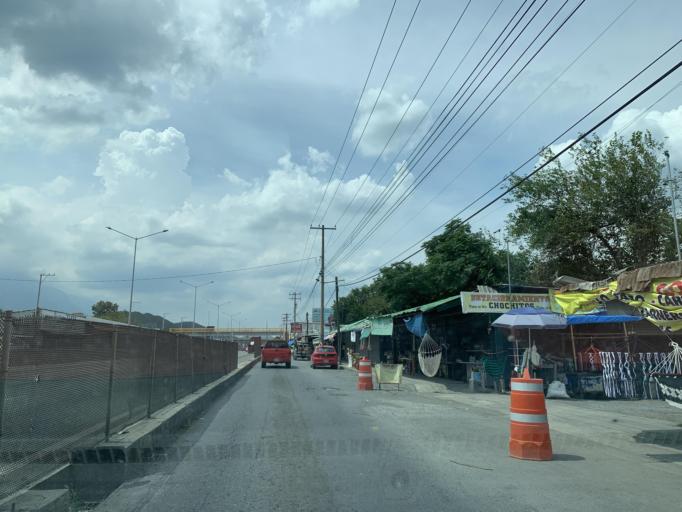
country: MX
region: Nuevo Leon
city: Santiago
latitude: 25.4490
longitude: -100.1605
